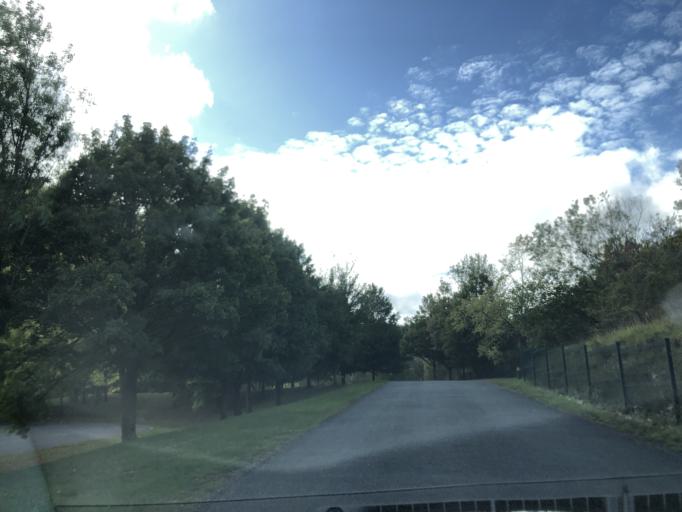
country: FR
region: Nord-Pas-de-Calais
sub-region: Departement du Pas-de-Calais
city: Wizernes
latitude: 50.7060
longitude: 2.2406
